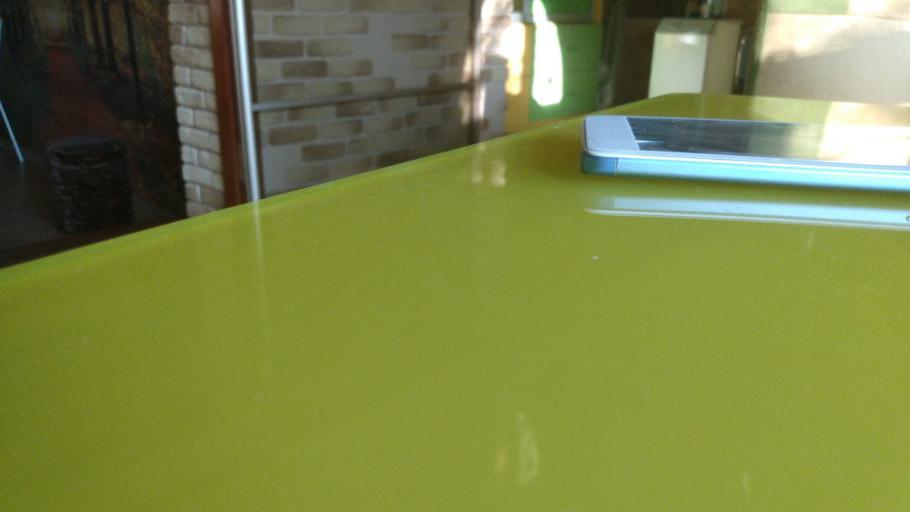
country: RU
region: Tverskaya
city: Vyshniy Volochek
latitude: 57.4512
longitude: 34.5729
